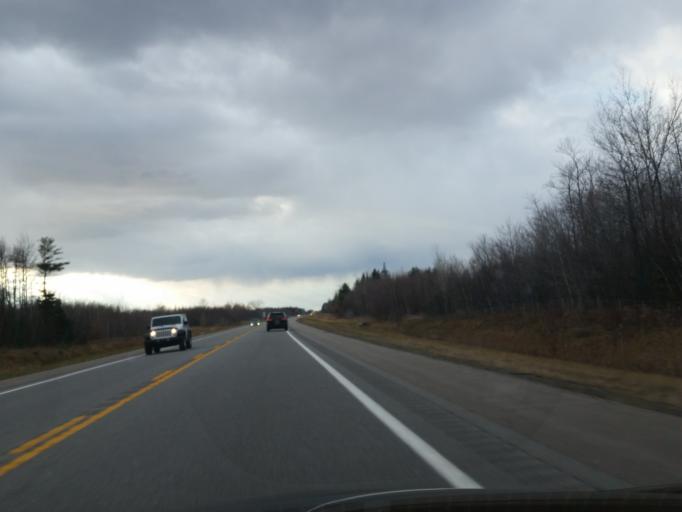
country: CA
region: Quebec
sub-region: Laurentides
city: Lachute
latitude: 45.6431
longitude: -74.2643
